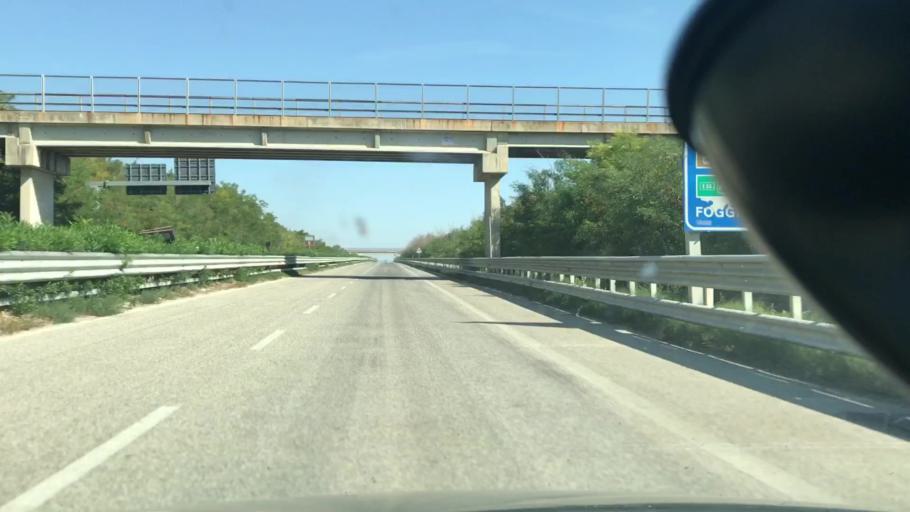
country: IT
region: Apulia
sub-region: Provincia di Foggia
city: Ordona
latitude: 41.3090
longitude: 15.5566
